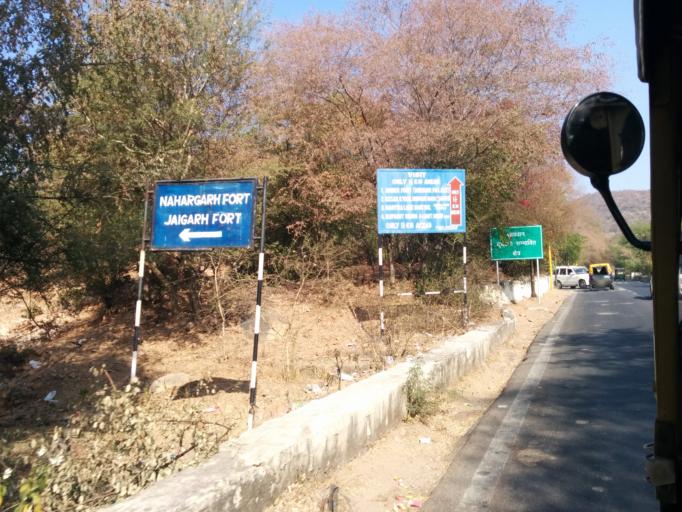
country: IN
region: Rajasthan
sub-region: Jaipur
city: Jaipur
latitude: 26.9674
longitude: 75.8473
